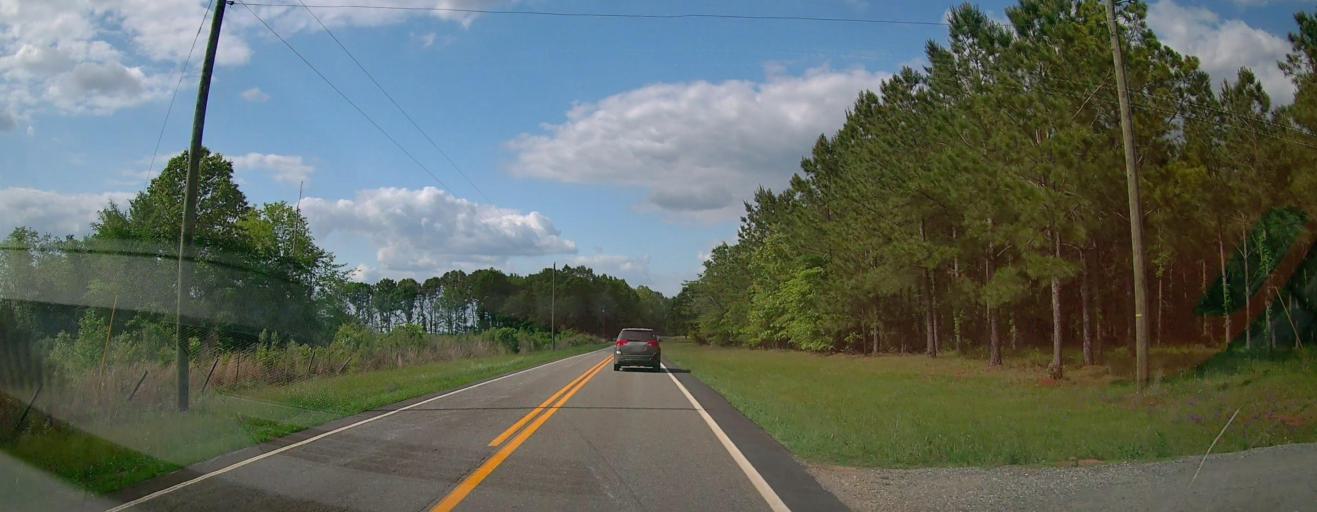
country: US
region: Georgia
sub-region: Laurens County
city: East Dublin
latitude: 32.6488
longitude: -82.8959
